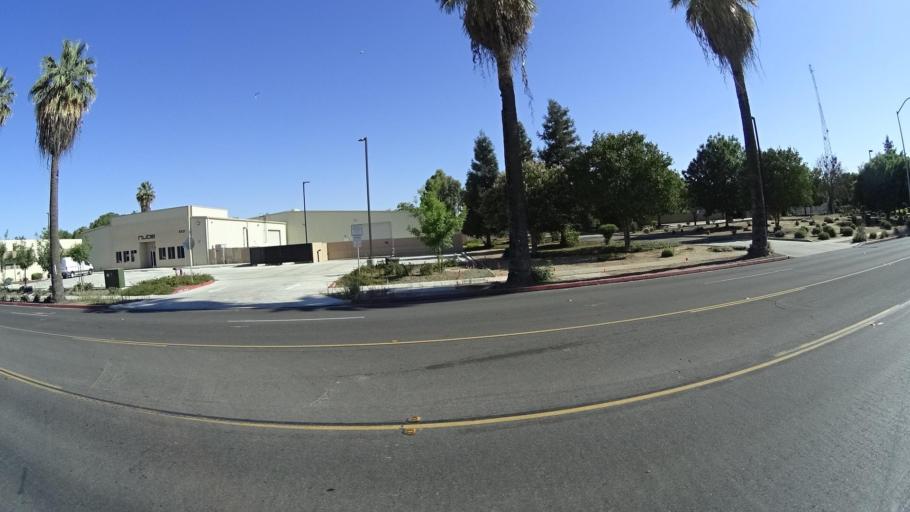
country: US
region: California
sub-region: Fresno County
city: Sunnyside
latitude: 36.7574
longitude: -119.7081
